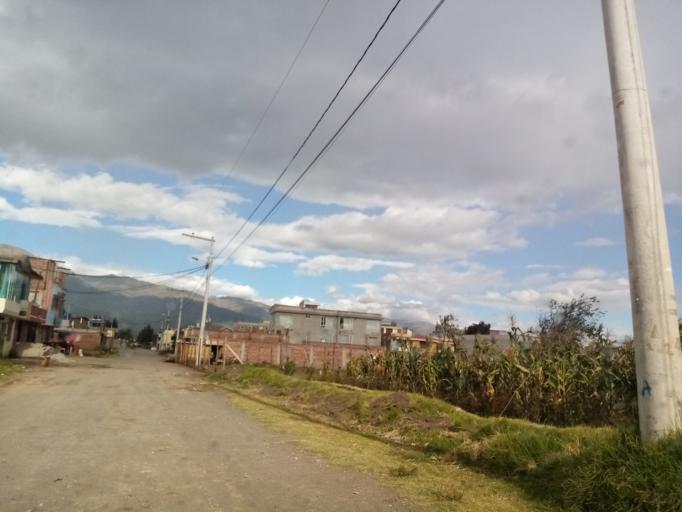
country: EC
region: Chimborazo
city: Riobamba
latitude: -1.6876
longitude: -78.6257
